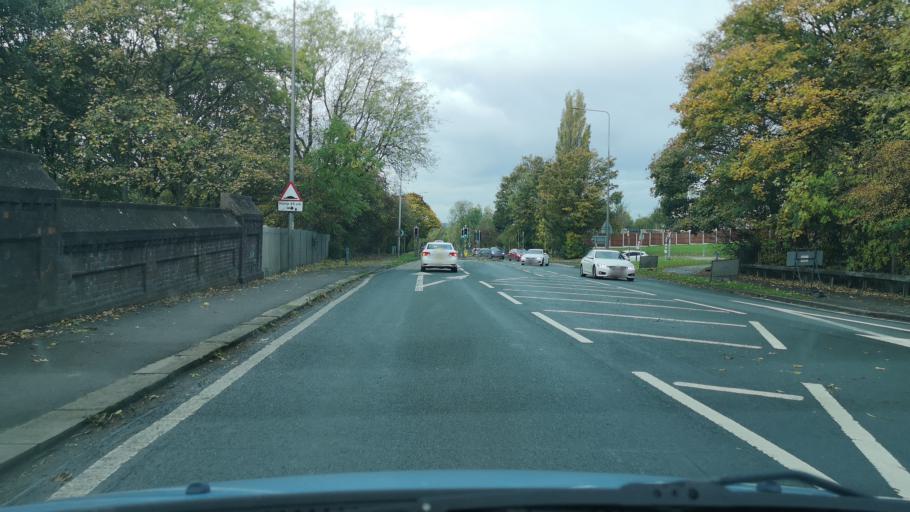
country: GB
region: England
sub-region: North Lincolnshire
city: Scunthorpe
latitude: 53.5848
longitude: -0.6729
